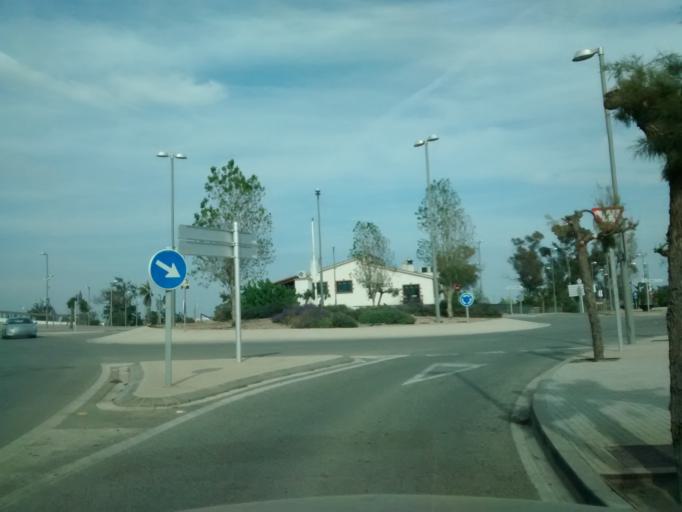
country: ES
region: Catalonia
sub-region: Provincia de Tarragona
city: Deltebre
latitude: 40.7112
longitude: 0.7163
